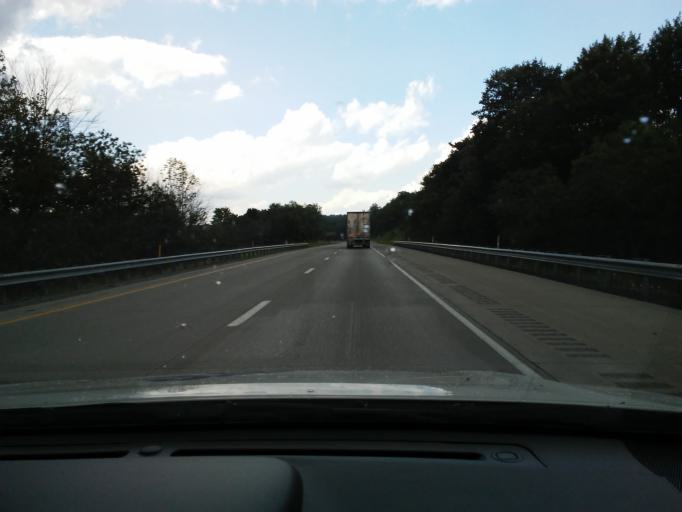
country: US
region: Pennsylvania
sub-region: Jefferson County
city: Falls Creek
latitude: 41.1571
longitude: -78.8181
